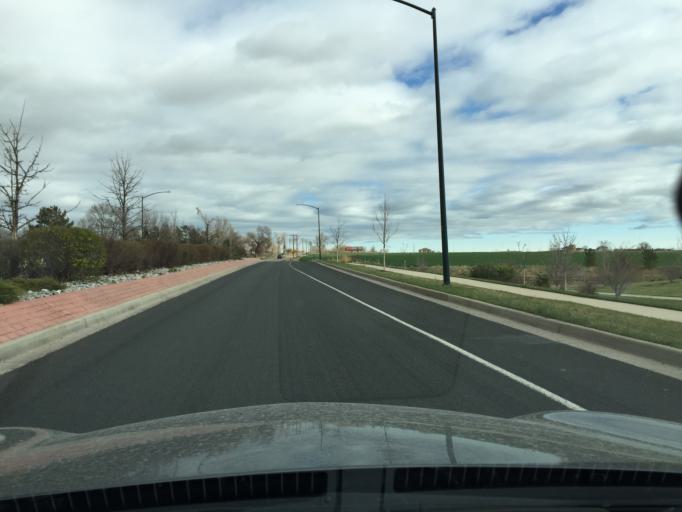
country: US
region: Colorado
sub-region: Adams County
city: Northglenn
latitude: 39.9674
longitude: -104.9969
